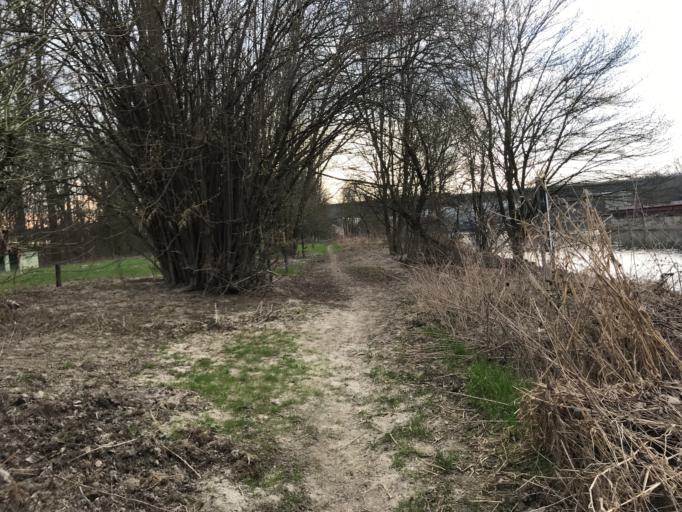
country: DE
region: Rheinland-Pfalz
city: Budenheim
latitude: 50.0316
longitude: 8.2158
